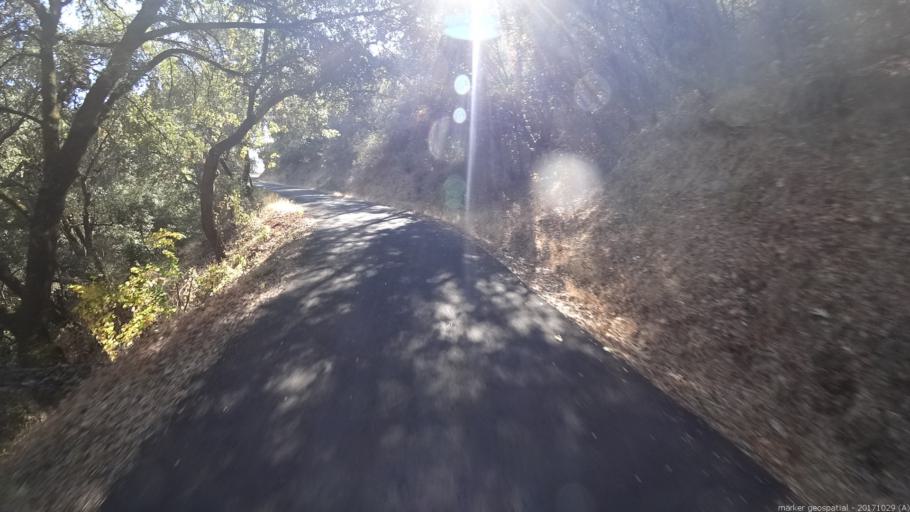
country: US
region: California
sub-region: Shasta County
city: Shasta
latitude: 40.4805
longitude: -122.6748
